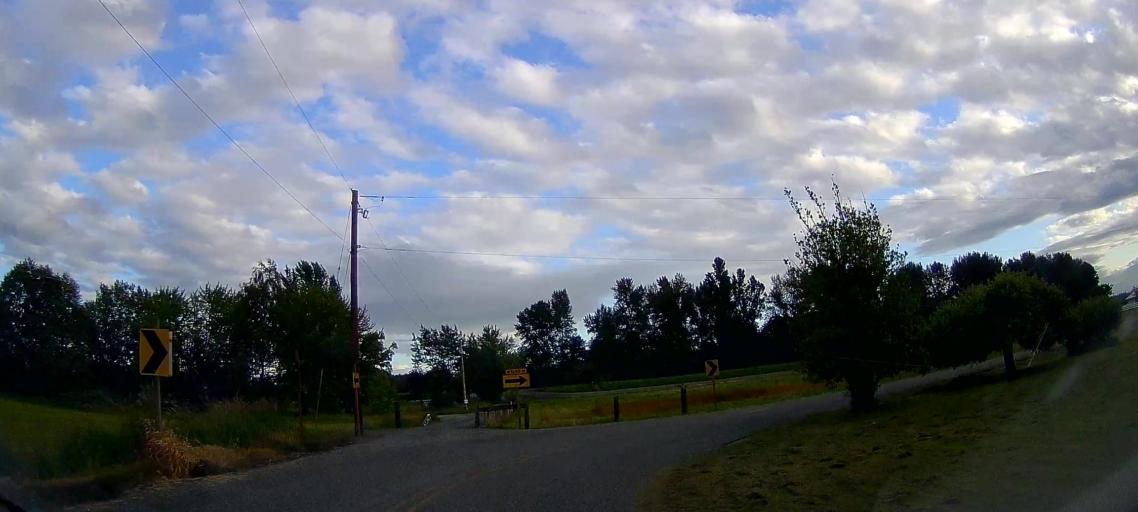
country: US
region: Washington
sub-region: Skagit County
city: Mount Vernon
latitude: 48.3850
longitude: -122.3836
